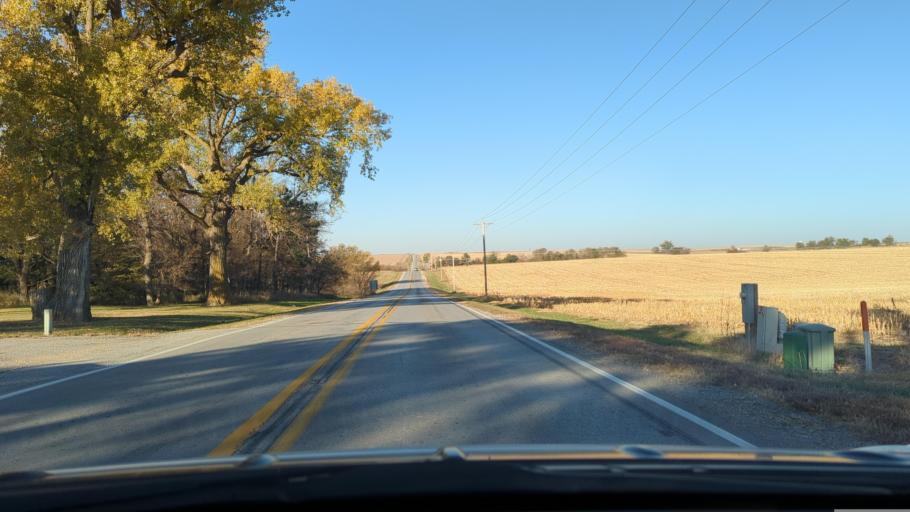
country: US
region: Nebraska
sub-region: Sarpy County
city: Springfield
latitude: 41.0890
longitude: -96.1581
